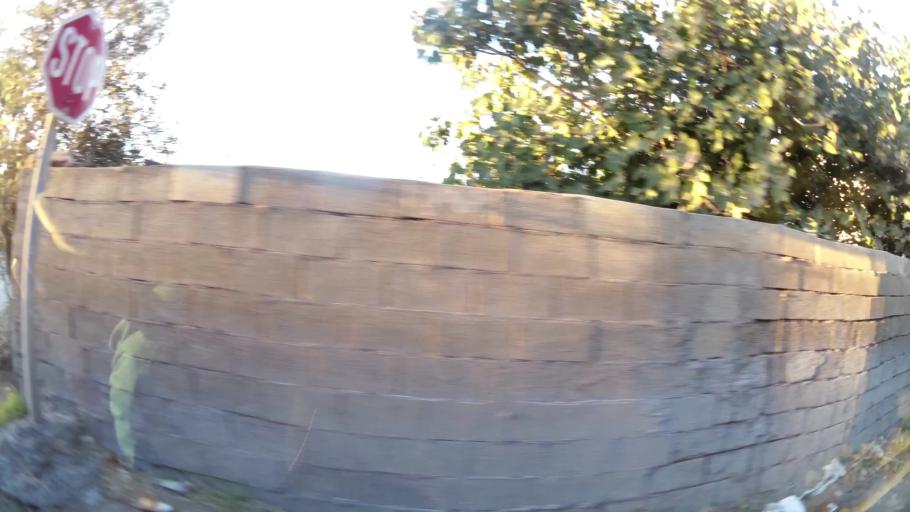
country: GR
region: Attica
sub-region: Nomarchia Athinas
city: Petroupolis
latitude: 38.0504
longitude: 23.6433
